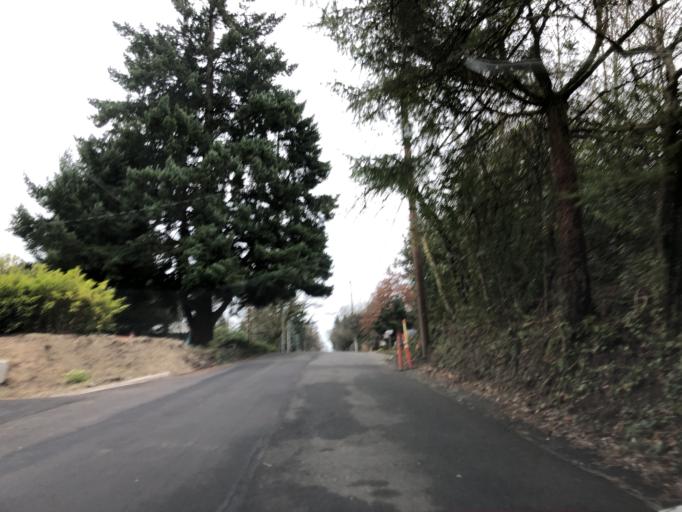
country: US
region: Oregon
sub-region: Washington County
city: Tigard
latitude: 45.4170
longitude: -122.7830
